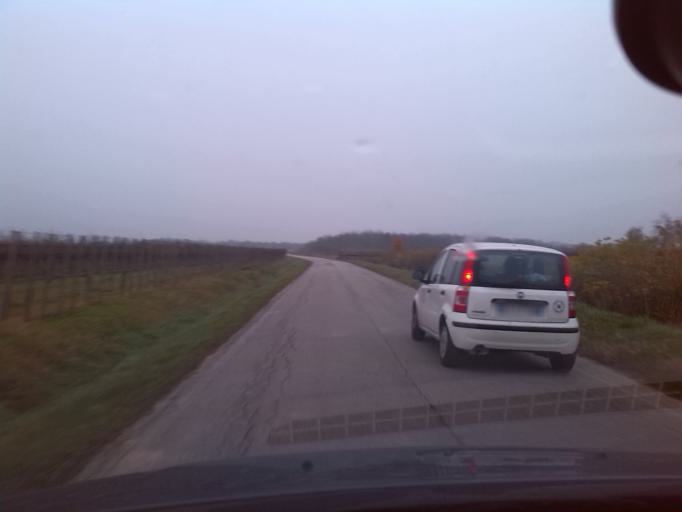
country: IT
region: Friuli Venezia Giulia
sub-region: Provincia di Gorizia
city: Moraro
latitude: 45.9335
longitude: 13.4794
